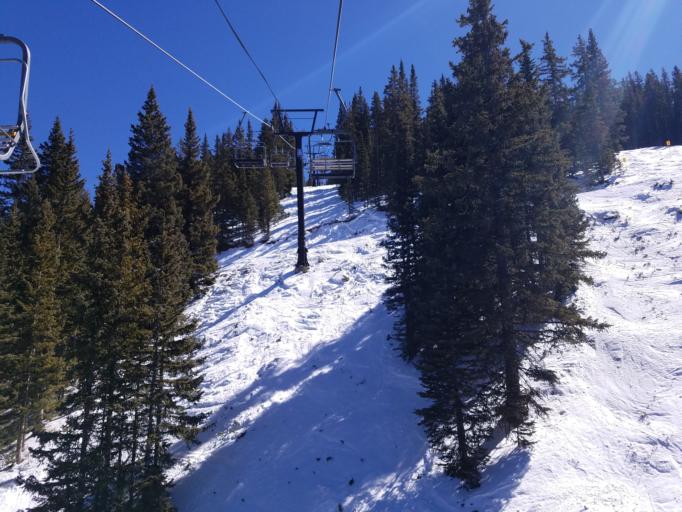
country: US
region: New Mexico
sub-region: Santa Fe County
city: Santa Fe
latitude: 35.7905
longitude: -105.7918
